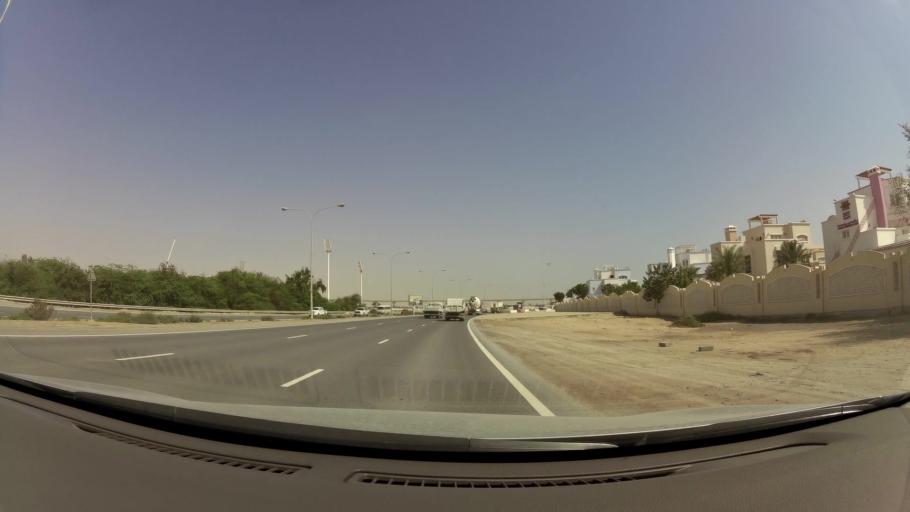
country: QA
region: Baladiyat ad Dawhah
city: Doha
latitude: 25.3722
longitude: 51.4972
